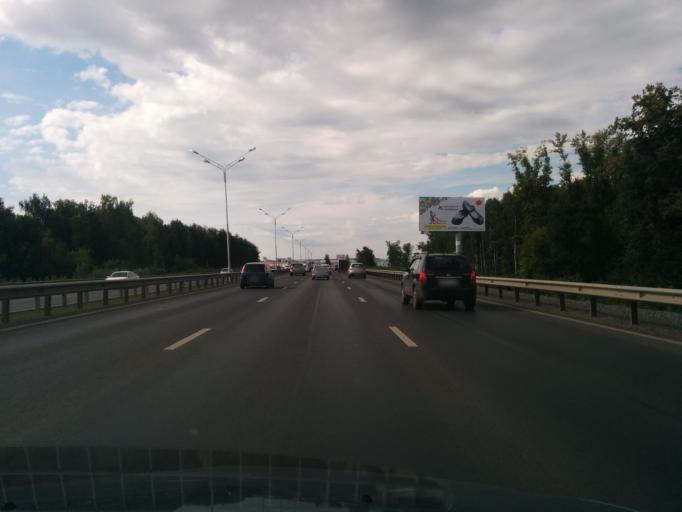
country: RU
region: Bashkortostan
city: Ufa
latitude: 54.6849
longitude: 55.9366
